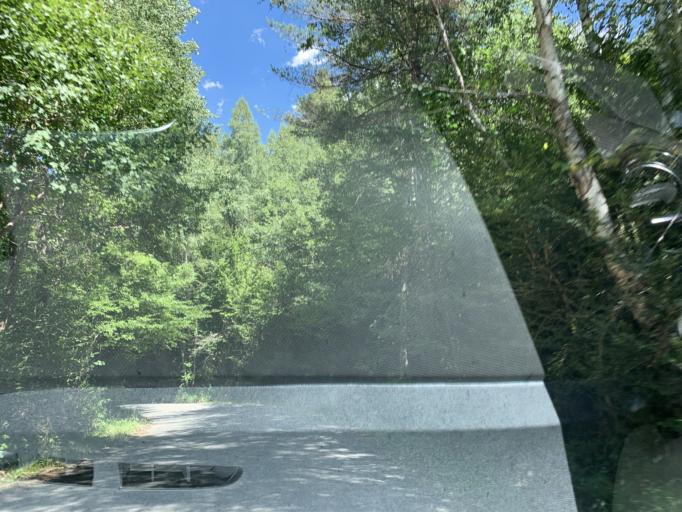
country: ES
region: Aragon
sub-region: Provincia de Huesca
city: Hoz de Jaca
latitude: 42.7041
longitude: -0.3041
